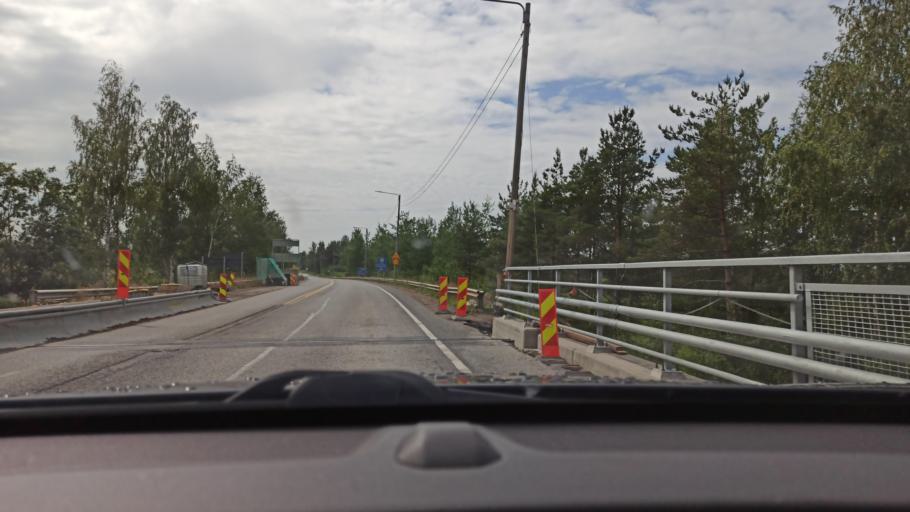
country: FI
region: Satakunta
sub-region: Pori
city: Pori
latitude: 61.5130
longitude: 21.7681
